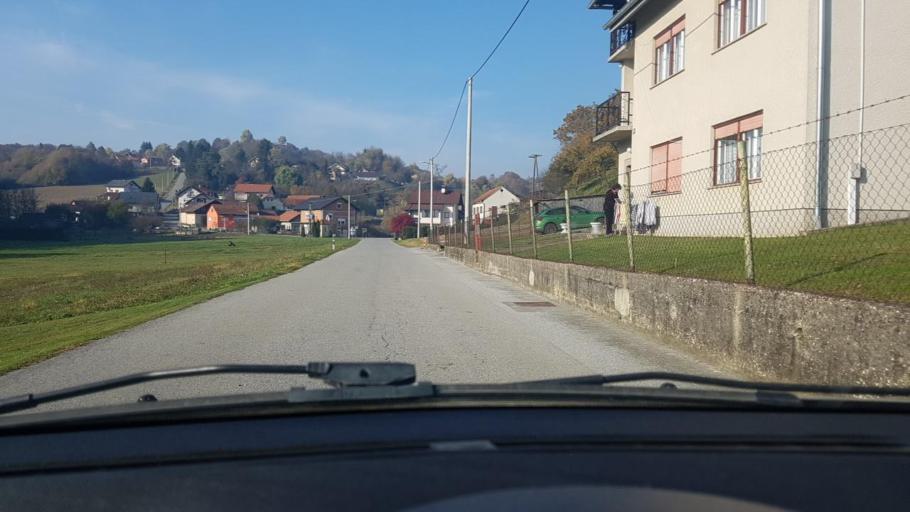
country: HR
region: Krapinsko-Zagorska
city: Zabok
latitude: 46.0296
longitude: 15.8845
